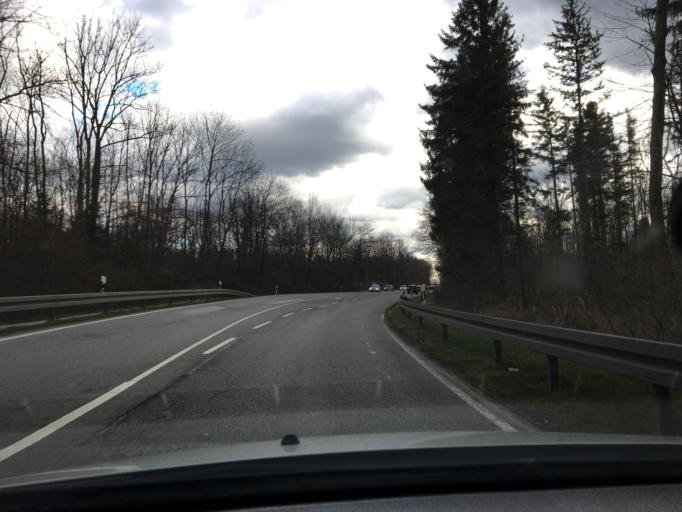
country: DE
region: Bavaria
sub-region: Upper Bavaria
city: Neufahrn bei Freising
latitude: 48.3127
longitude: 11.7029
